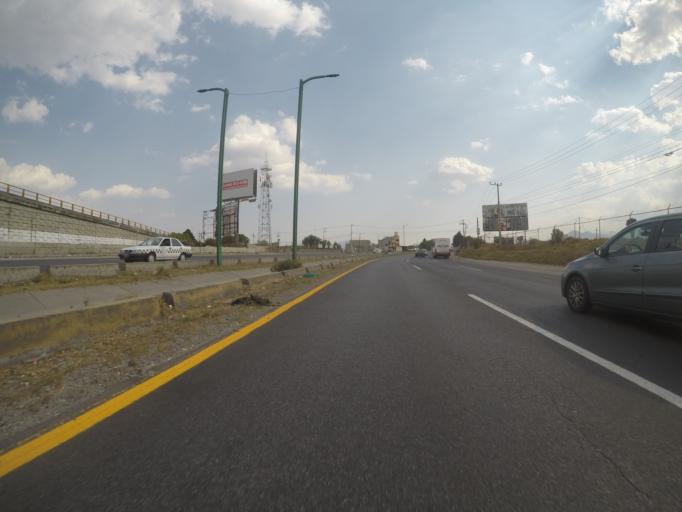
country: MX
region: Mexico
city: San Mateo Mexicaltzingo
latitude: 19.2160
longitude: -99.5909
